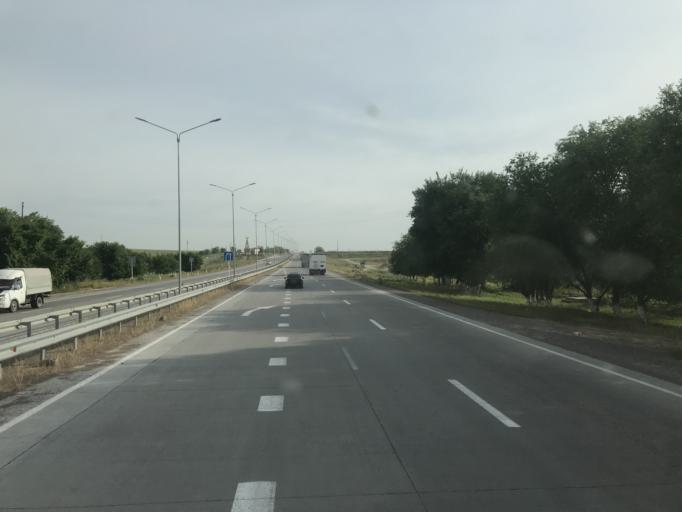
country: KZ
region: Ongtustik Qazaqstan
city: Qazyqurt
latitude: 41.7997
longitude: 69.3942
